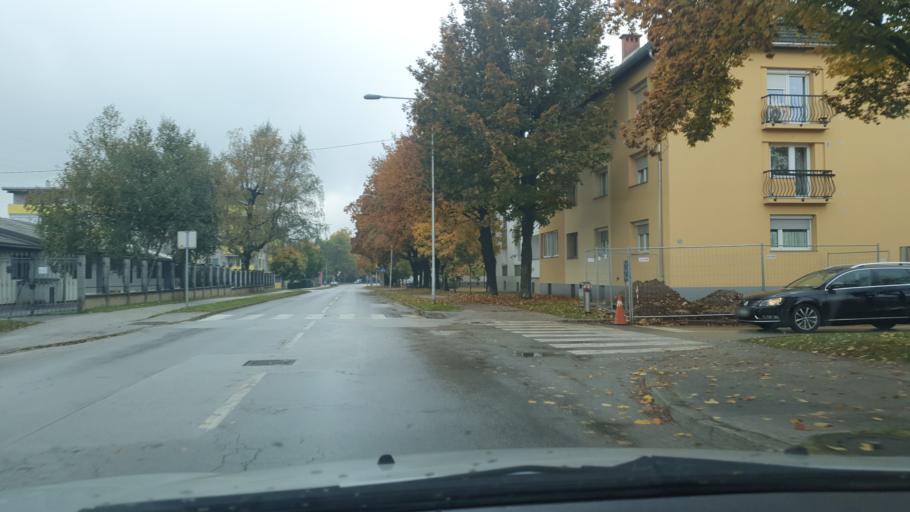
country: SI
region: Kranj
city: Kranj
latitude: 46.2341
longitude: 14.3663
